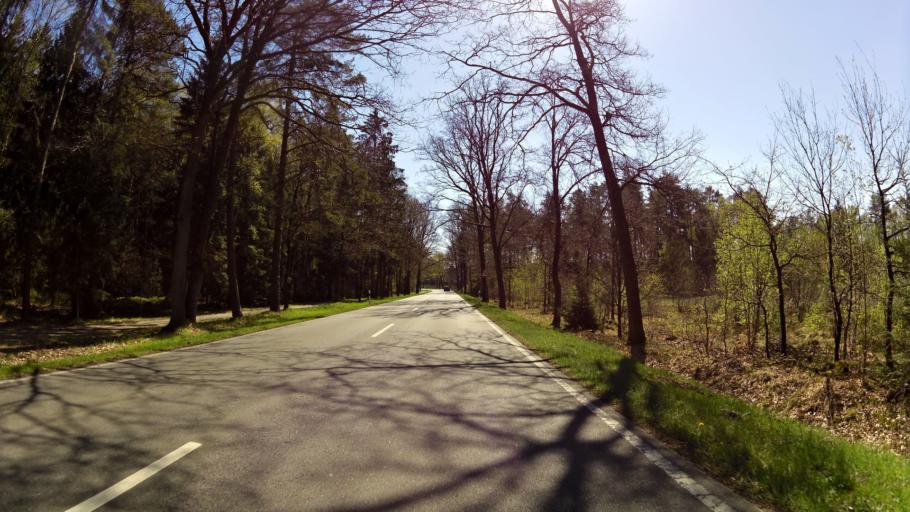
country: DE
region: Lower Saxony
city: Soltau
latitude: 53.0159
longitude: 9.7772
